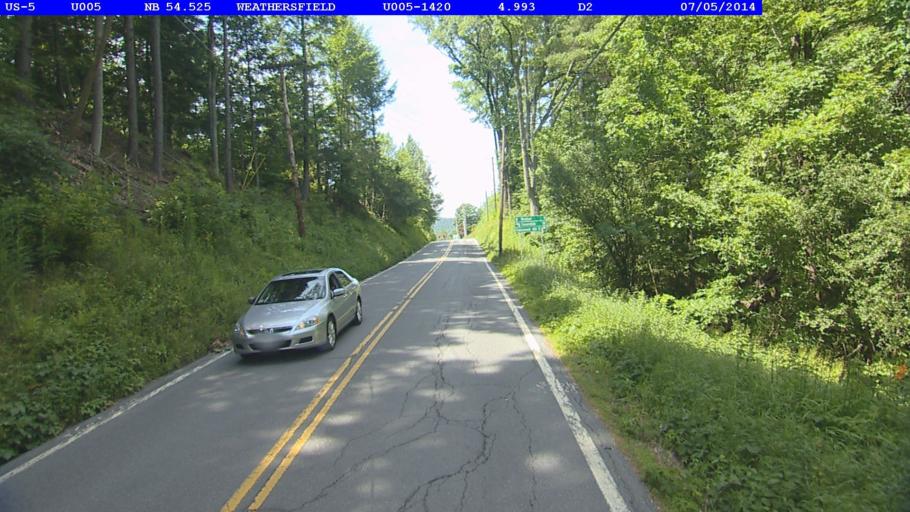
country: US
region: New Hampshire
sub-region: Sullivan County
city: Claremont
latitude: 43.4042
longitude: -72.4066
